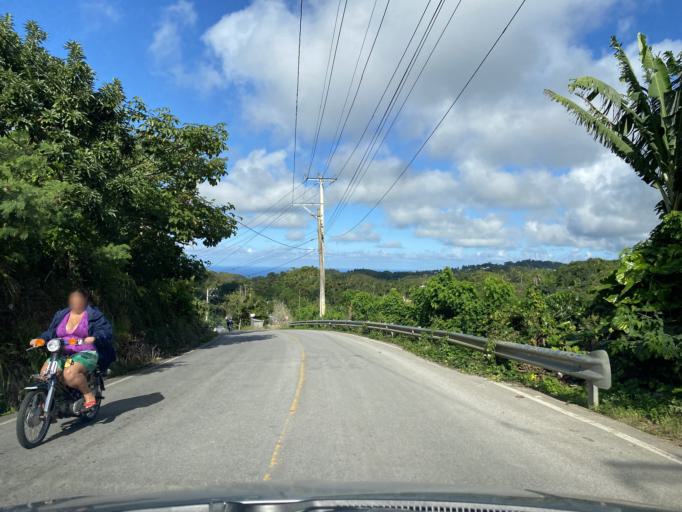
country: DO
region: Samana
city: Sanchez
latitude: 19.2597
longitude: -69.5699
